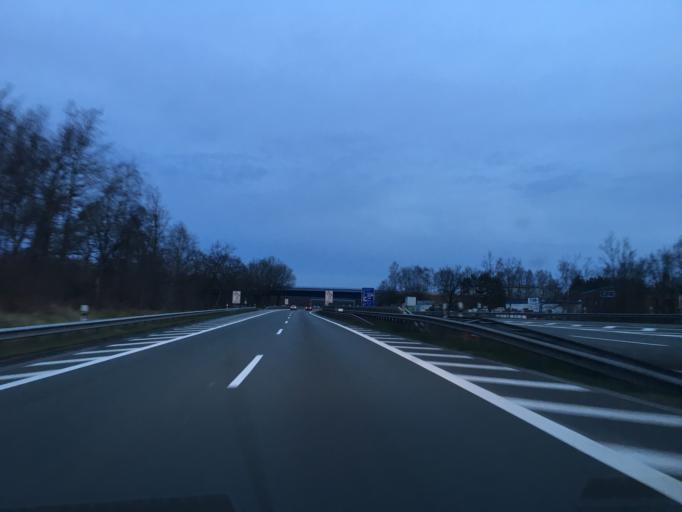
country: DE
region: Lower Saxony
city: Harmstorf
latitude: 53.3843
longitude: 10.0207
